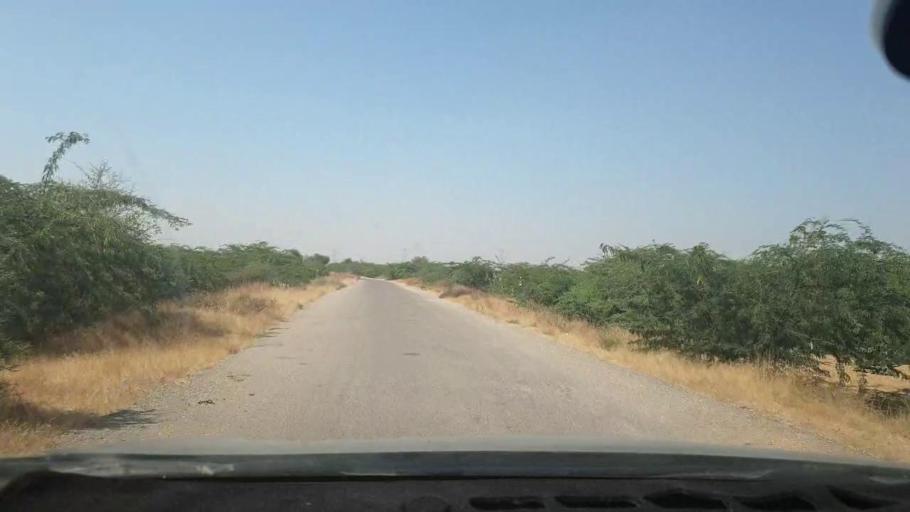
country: PK
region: Sindh
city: Malir Cantonment
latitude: 25.1574
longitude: 67.1426
